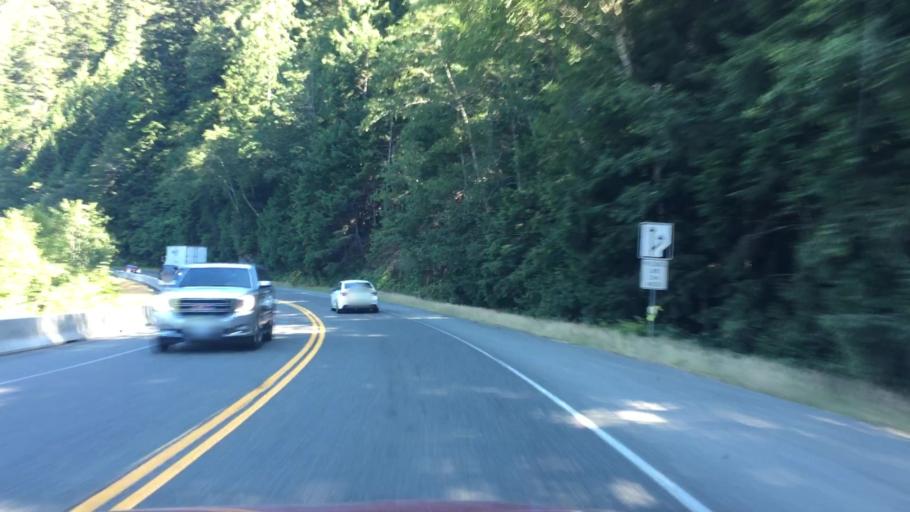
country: CA
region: British Columbia
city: Port Alberni
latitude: 49.2859
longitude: -124.5931
